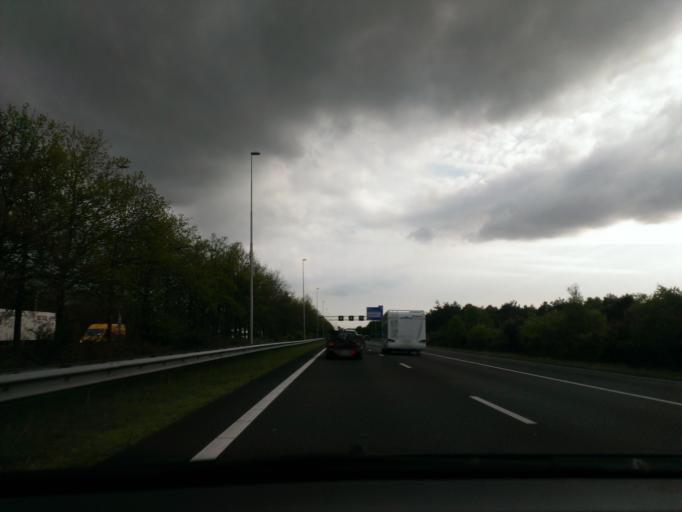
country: NL
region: Gelderland
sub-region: Gemeente Rozendaal
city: Rozendaal
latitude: 52.0524
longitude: 5.9374
